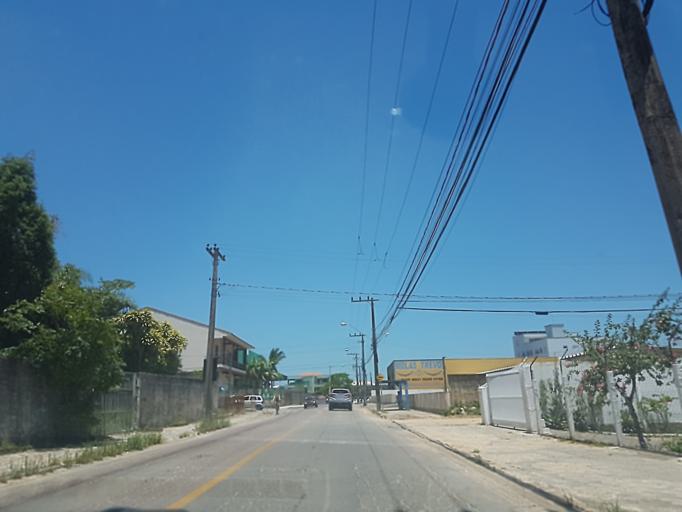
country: BR
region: Santa Catarina
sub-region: Tubarao
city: Tubarao
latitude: -28.4743
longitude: -49.0315
